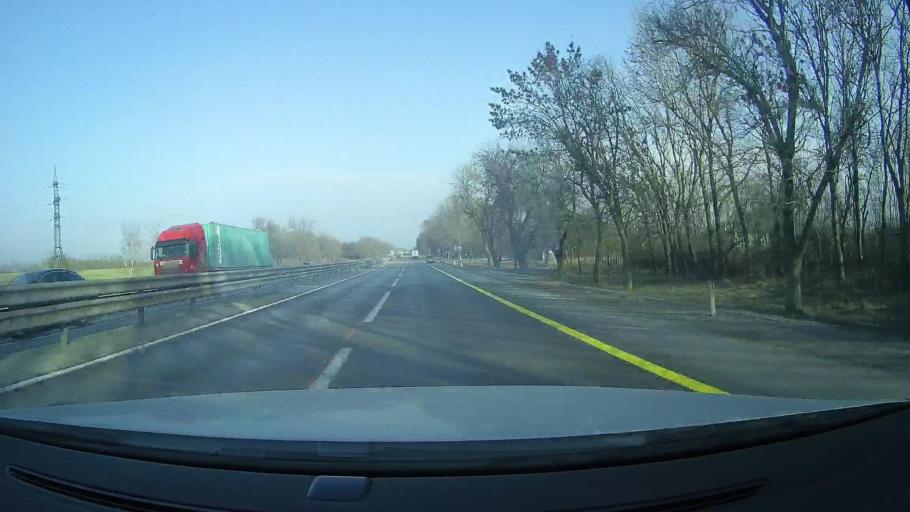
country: RU
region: Rostov
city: Aksay
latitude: 47.3292
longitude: 39.8650
